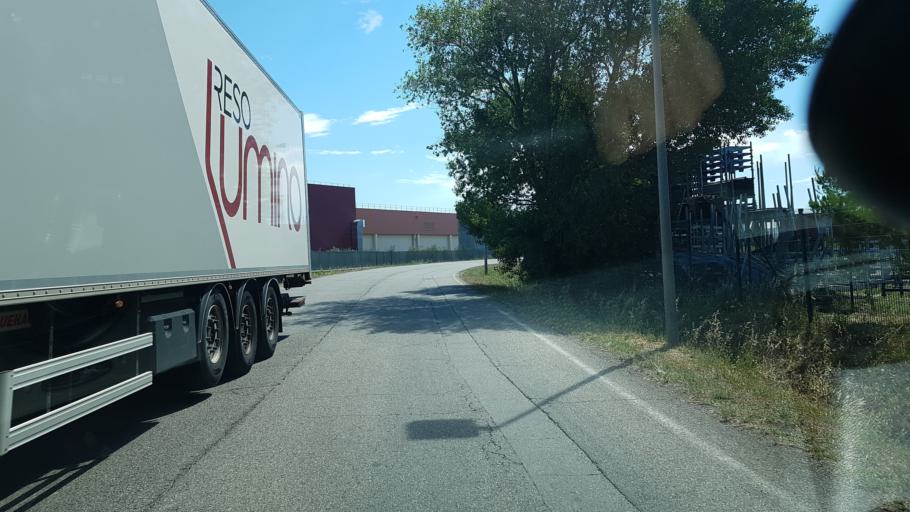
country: FR
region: Provence-Alpes-Cote d'Azur
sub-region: Departement des Bouches-du-Rhone
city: Saint-Martin-de-Crau
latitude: 43.6263
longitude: 4.8009
